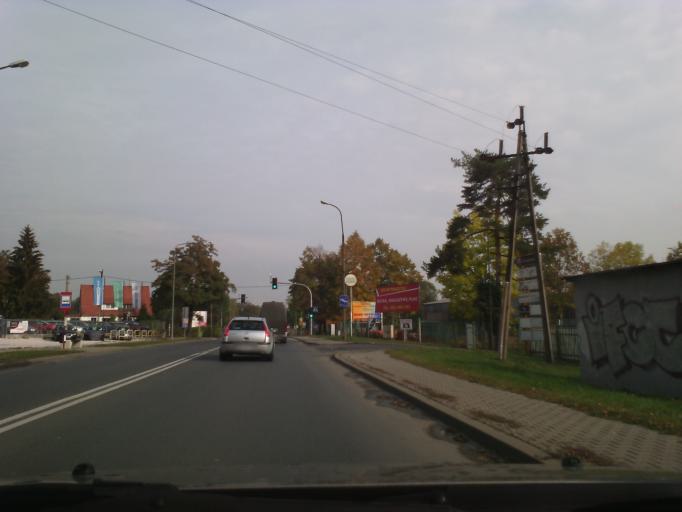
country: PL
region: Lower Silesian Voivodeship
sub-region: Jelenia Gora
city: Jelenia Gora
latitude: 50.8942
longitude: 15.7128
